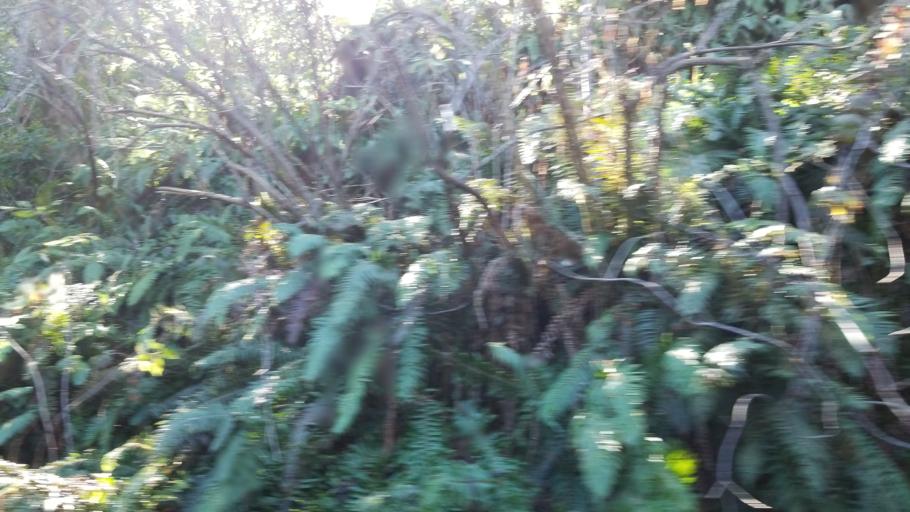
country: US
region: California
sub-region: Mendocino County
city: Fort Bragg
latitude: 39.4464
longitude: -123.7918
